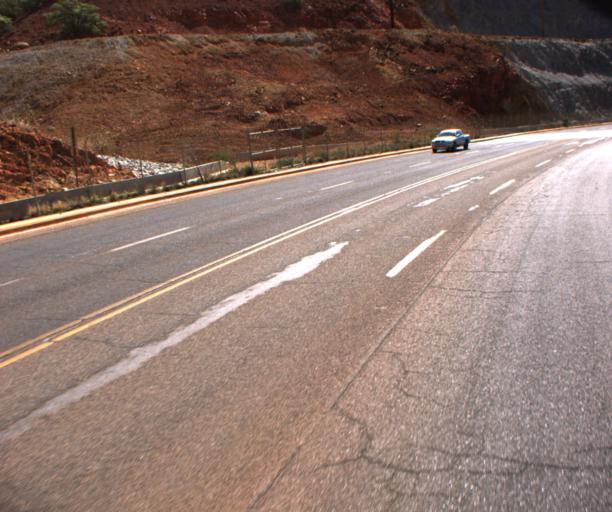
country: US
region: Arizona
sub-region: Cochise County
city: Bisbee
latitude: 31.4401
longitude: -109.9090
